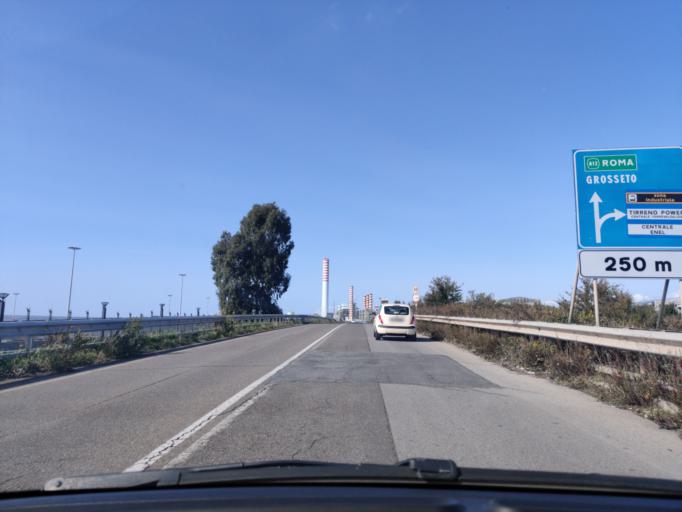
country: IT
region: Latium
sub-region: Citta metropolitana di Roma Capitale
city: Aurelia
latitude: 42.1143
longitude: 11.7737
